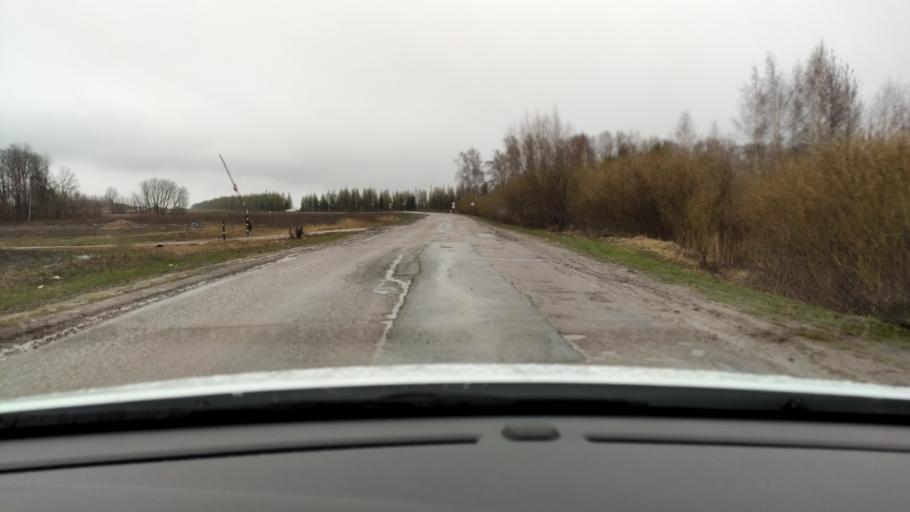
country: RU
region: Tatarstan
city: Vysokaya Gora
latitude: 55.8951
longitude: 49.3328
